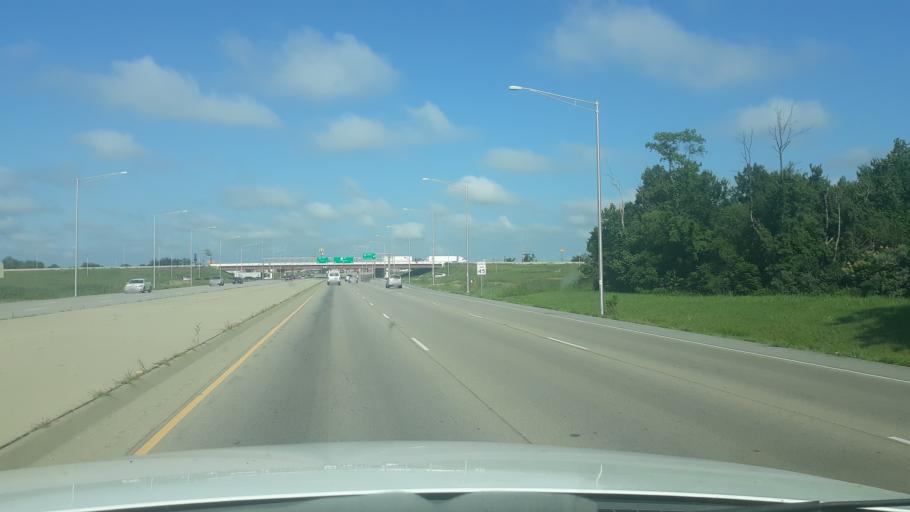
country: US
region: Illinois
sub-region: Williamson County
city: Marion
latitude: 37.7407
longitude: -88.9528
